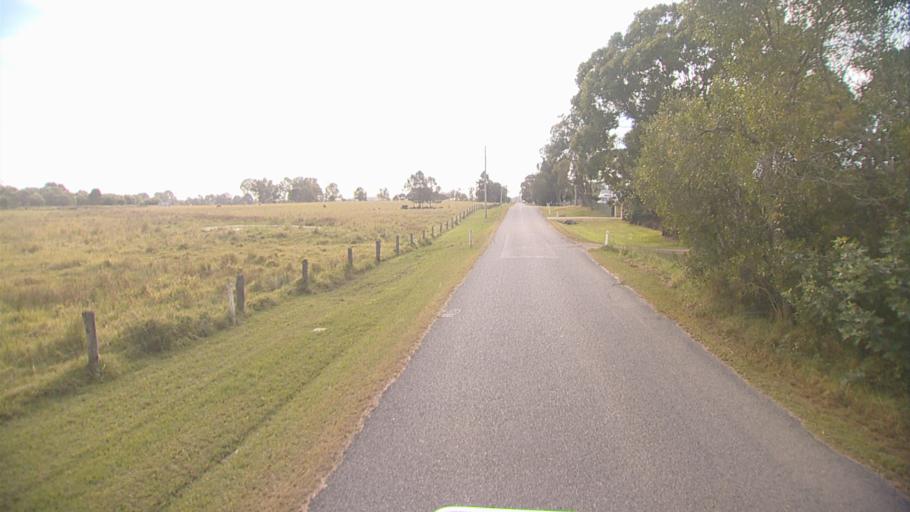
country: AU
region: Queensland
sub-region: Logan
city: Waterford West
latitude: -27.6816
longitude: 153.1585
